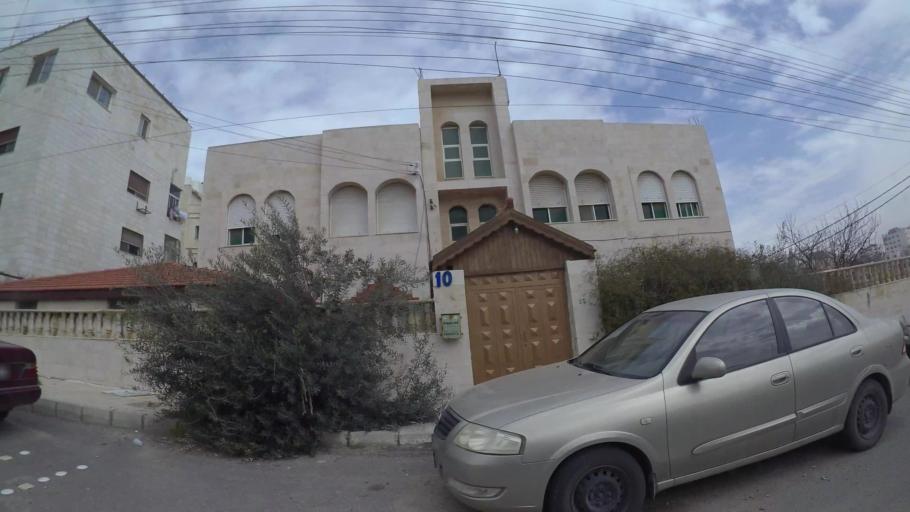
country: JO
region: Amman
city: Umm as Summaq
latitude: 31.9076
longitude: 35.8464
